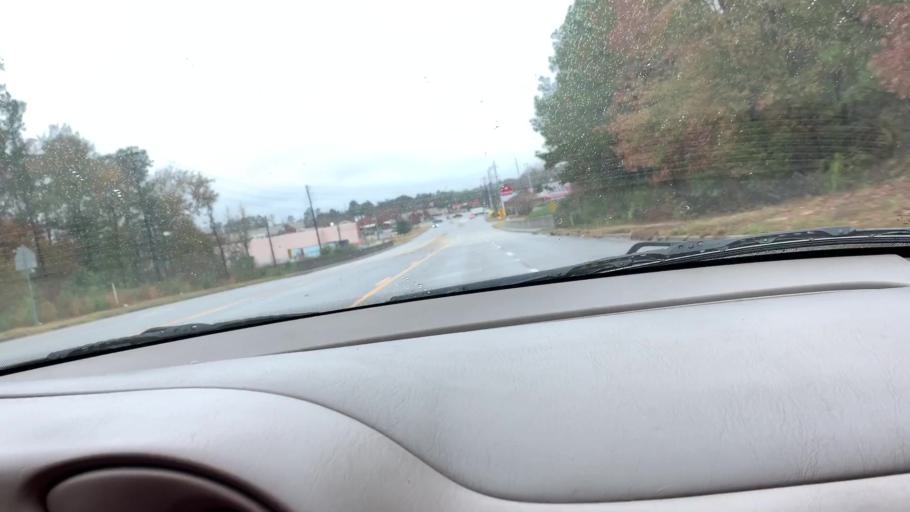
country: US
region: South Carolina
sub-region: Richland County
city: Dentsville
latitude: 34.0653
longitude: -80.9519
